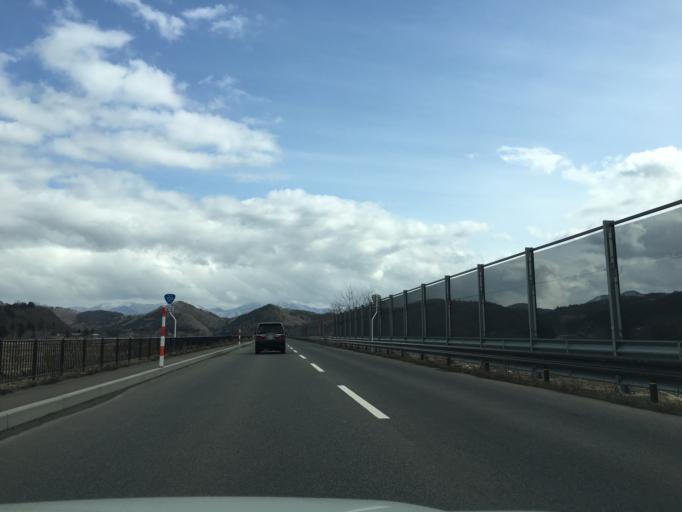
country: JP
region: Akita
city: Hanawa
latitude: 40.2304
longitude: 140.7057
